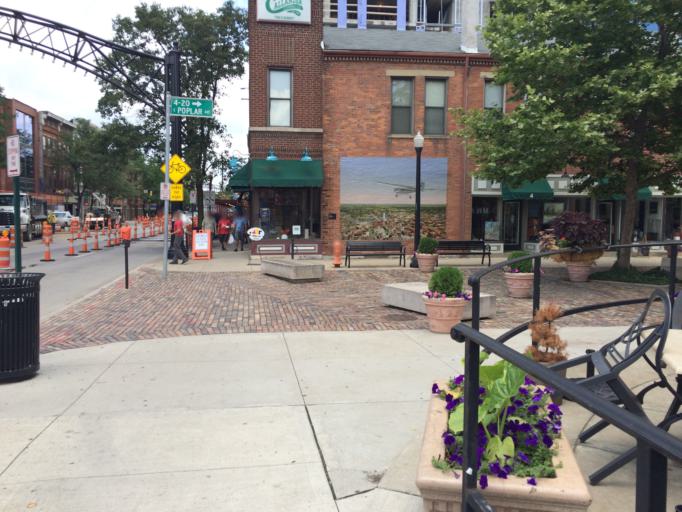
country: US
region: Ohio
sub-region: Franklin County
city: Columbus
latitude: 39.9746
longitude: -83.0030
